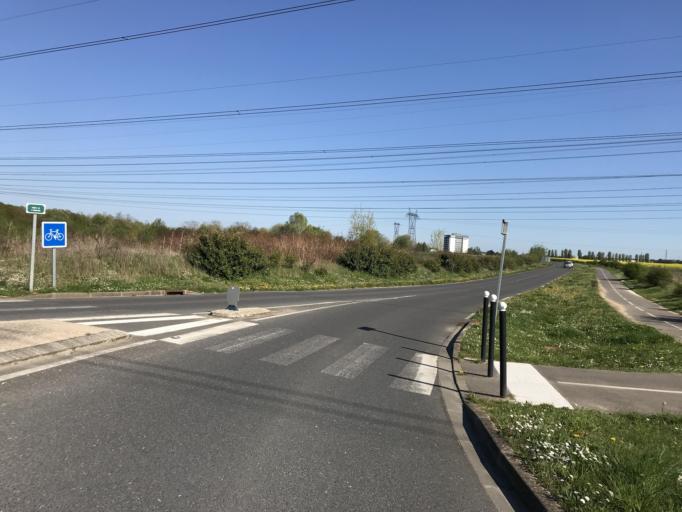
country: FR
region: Ile-de-France
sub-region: Departement de l'Essonne
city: Villejust
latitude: 48.6725
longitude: 2.2248
